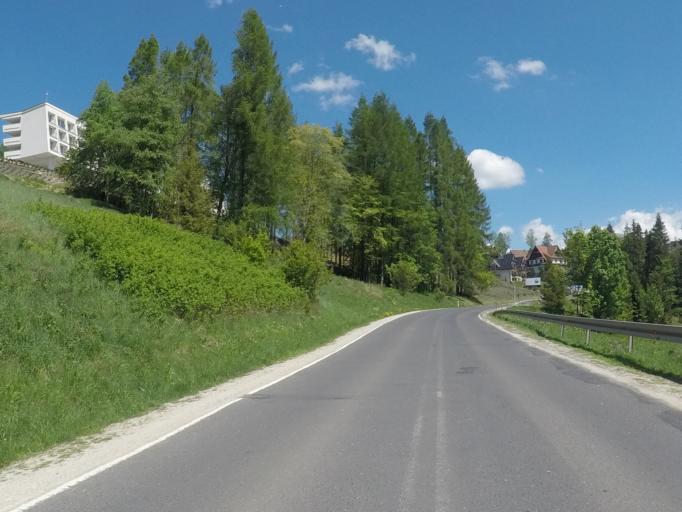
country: PL
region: Lesser Poland Voivodeship
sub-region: Powiat tatrzanski
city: Bukowina Tatrzanska
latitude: 49.3311
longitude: 20.0892
